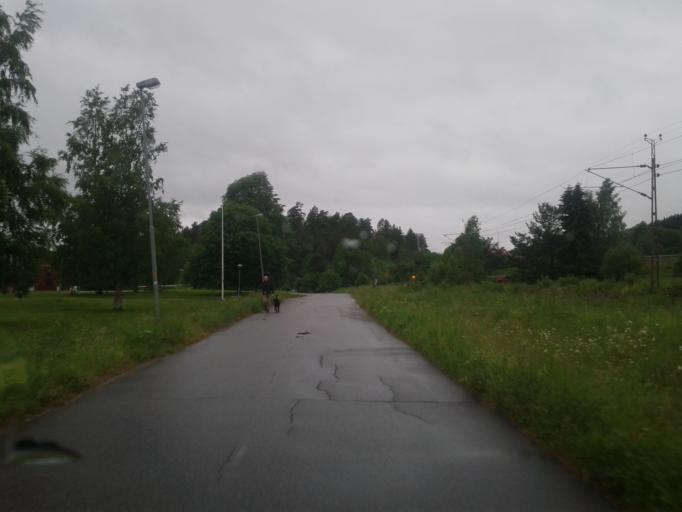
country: SE
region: Vaesternorrland
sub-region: Ange Kommun
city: Fransta
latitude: 62.4165
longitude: 16.5723
